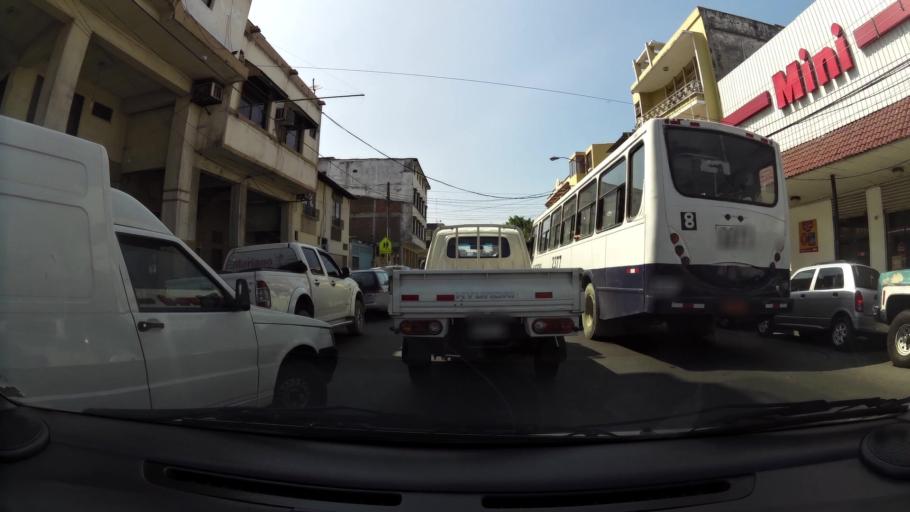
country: EC
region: Guayas
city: Guayaquil
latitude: -2.1922
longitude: -79.8930
